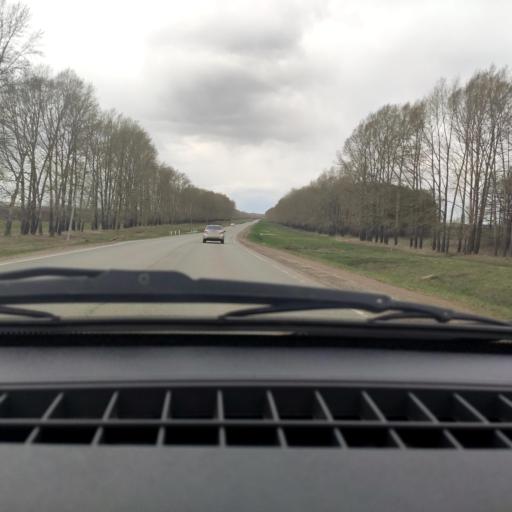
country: RU
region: Bashkortostan
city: Kushnarenkovo
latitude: 55.0816
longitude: 55.3658
